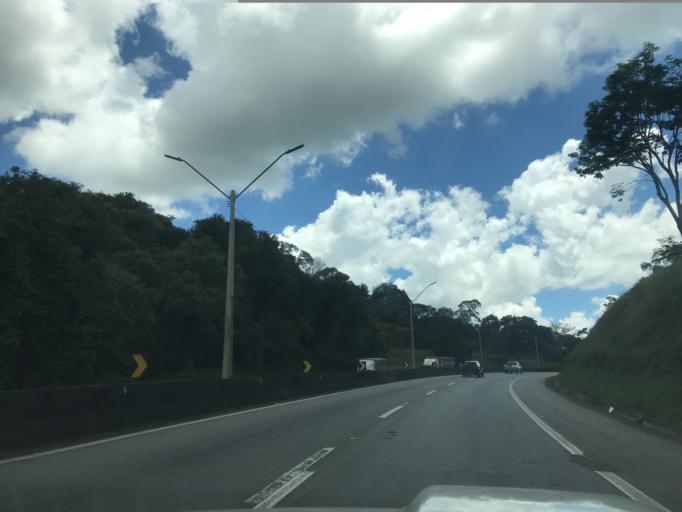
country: BR
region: Minas Gerais
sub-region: Tres Coracoes
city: Tres Coracoes
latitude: -21.5538
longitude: -45.2448
